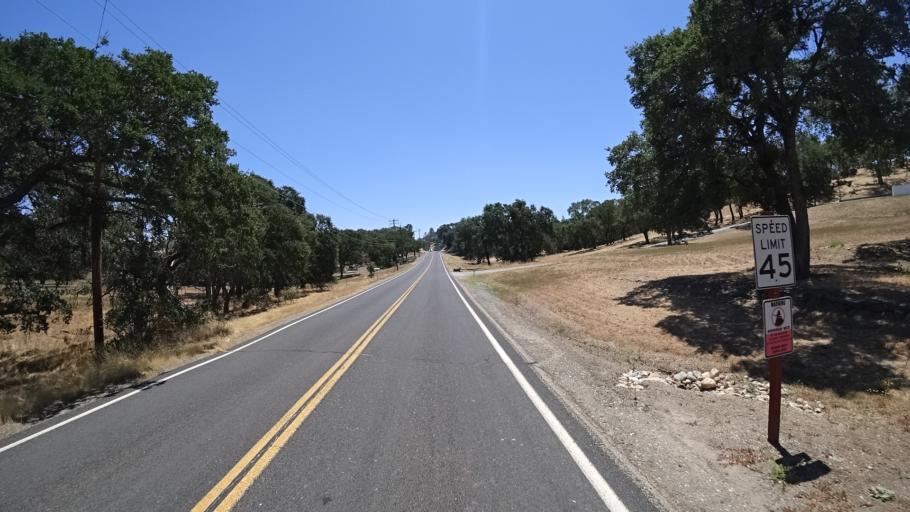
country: US
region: California
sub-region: Calaveras County
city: Rancho Calaveras
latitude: 38.1346
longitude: -120.8474
